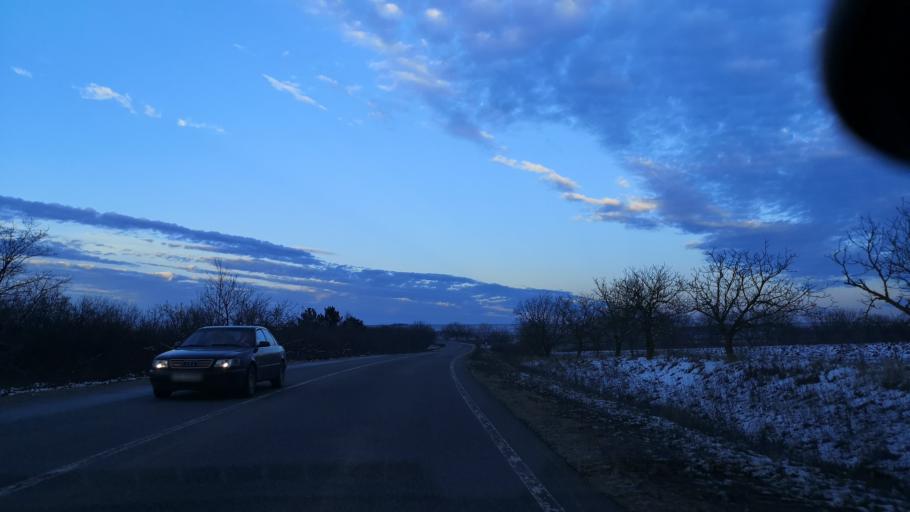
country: MD
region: Orhei
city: Orhei
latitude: 47.5559
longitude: 28.7965
